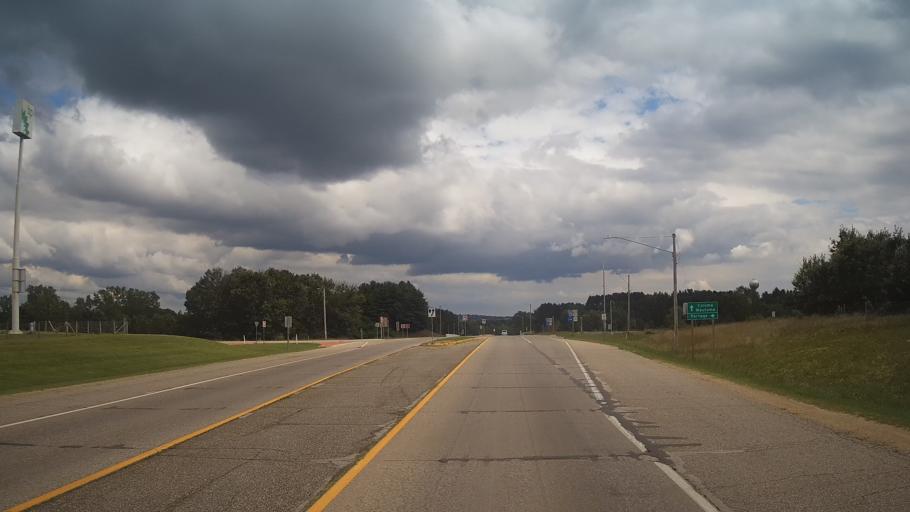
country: US
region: Wisconsin
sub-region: Marquette County
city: Westfield
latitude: 44.0347
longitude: -89.5322
